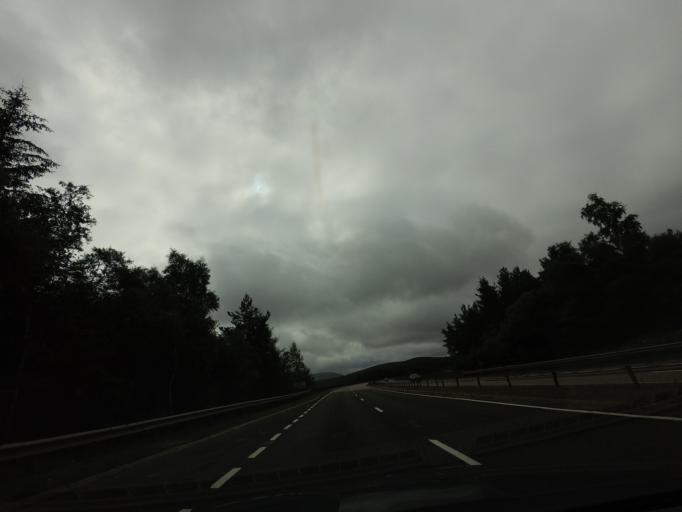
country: GB
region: Scotland
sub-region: Highland
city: Aviemore
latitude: 57.3372
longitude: -3.9830
